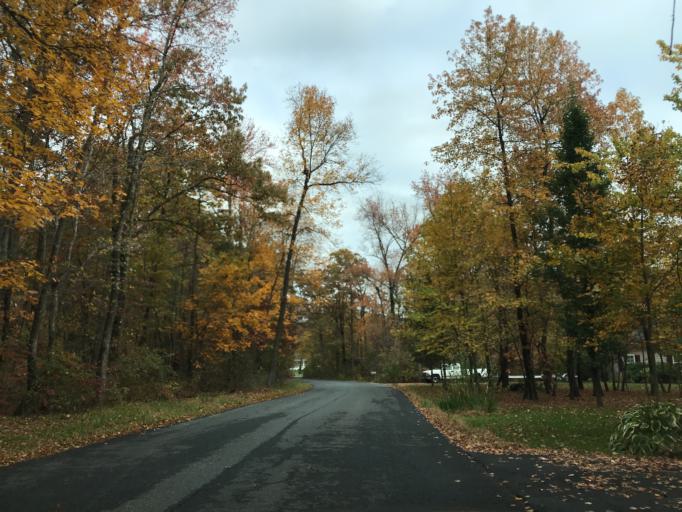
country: US
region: Maryland
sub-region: Baltimore County
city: Bowleys Quarters
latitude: 39.3211
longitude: -76.3949
